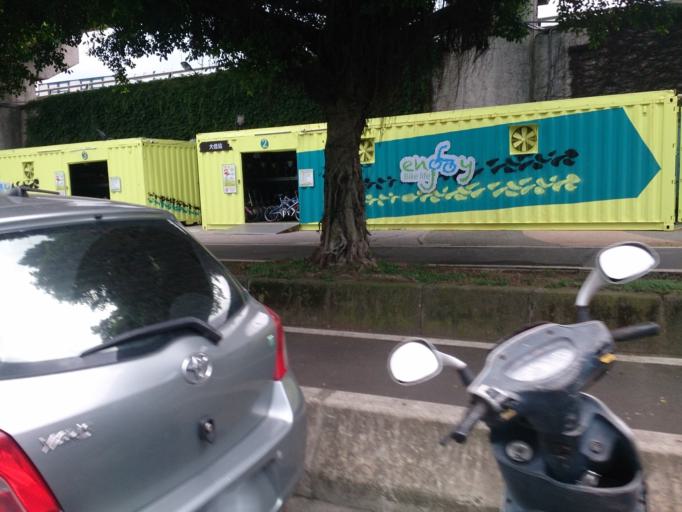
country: TW
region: Taipei
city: Taipei
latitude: 25.0737
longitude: 121.5405
